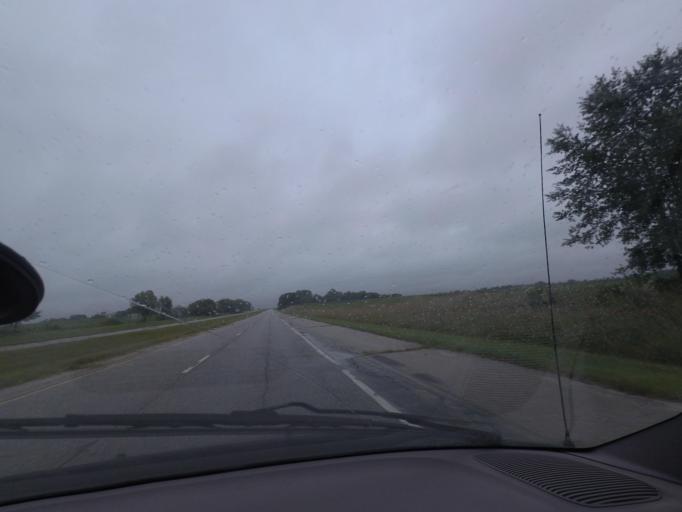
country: US
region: Illinois
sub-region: Pike County
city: Pittsfield
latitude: 39.6701
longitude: -90.8157
